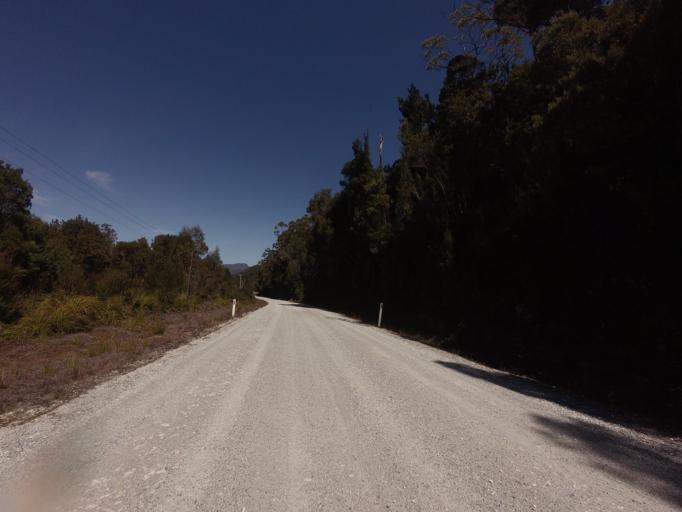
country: AU
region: Tasmania
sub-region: West Coast
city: Queenstown
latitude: -42.7589
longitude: 145.9853
